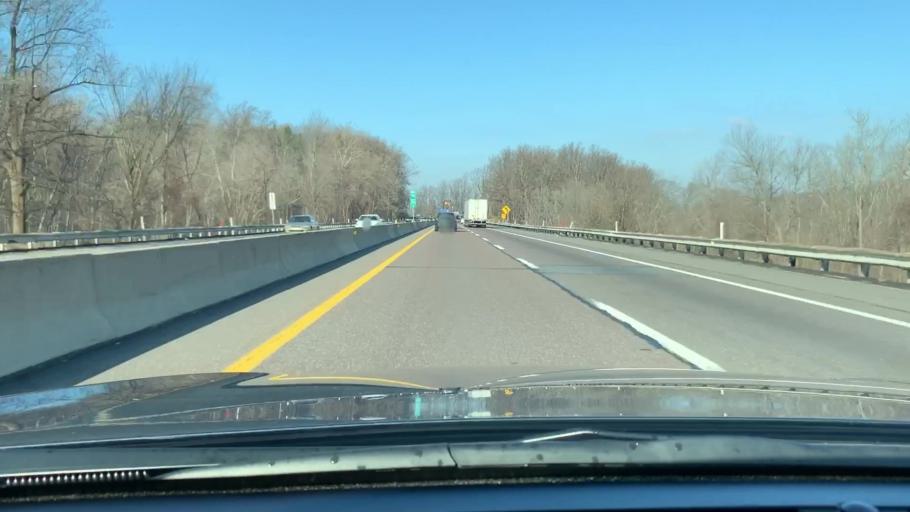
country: US
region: Pennsylvania
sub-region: Chester County
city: Elverson
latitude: 40.1108
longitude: -75.7596
